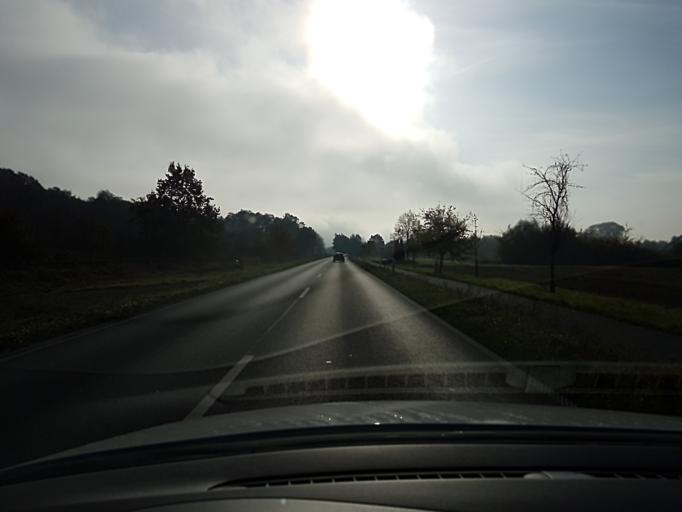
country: DE
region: Bavaria
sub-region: Regierungsbezirk Unterfranken
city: Sulzbach am Main
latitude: 49.8992
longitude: 9.1518
